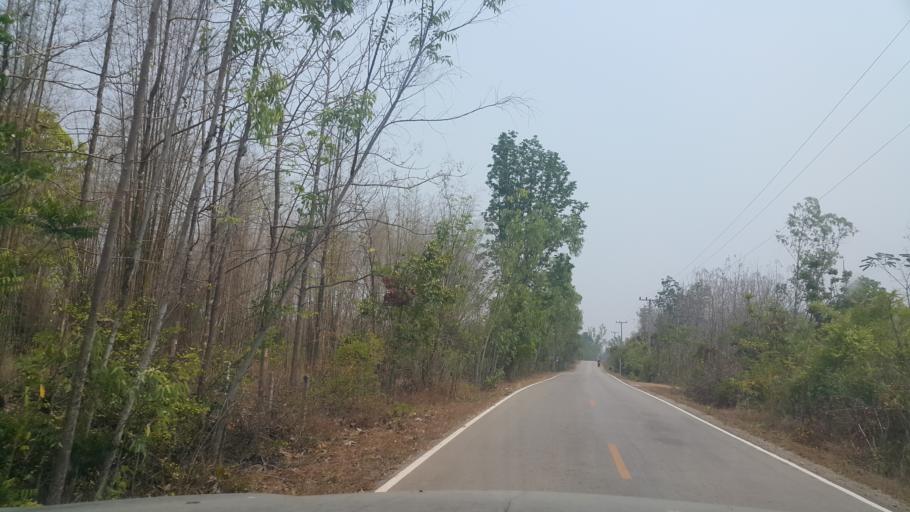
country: TH
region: Lampang
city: Sop Prap
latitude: 17.8959
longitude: 99.3155
